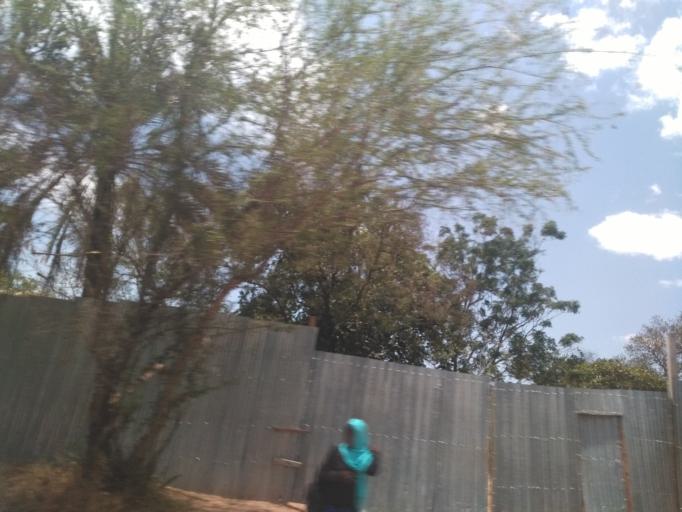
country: TZ
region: Mwanza
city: Mwanza
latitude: -2.5044
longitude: 32.9028
